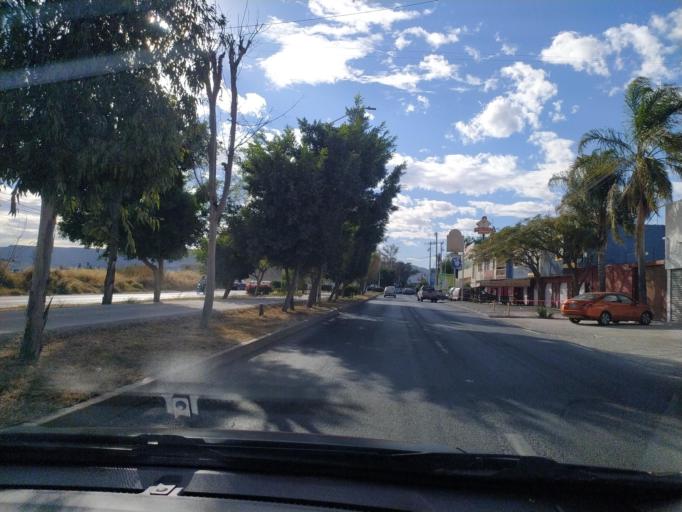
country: LA
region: Oudomxai
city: Muang La
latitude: 21.0289
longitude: 101.8498
